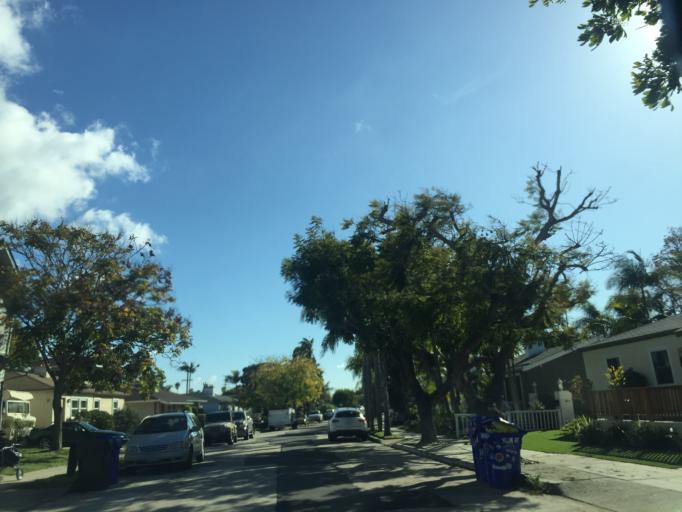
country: US
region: California
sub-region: San Diego County
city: La Jolla
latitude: 32.7862
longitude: -117.2359
